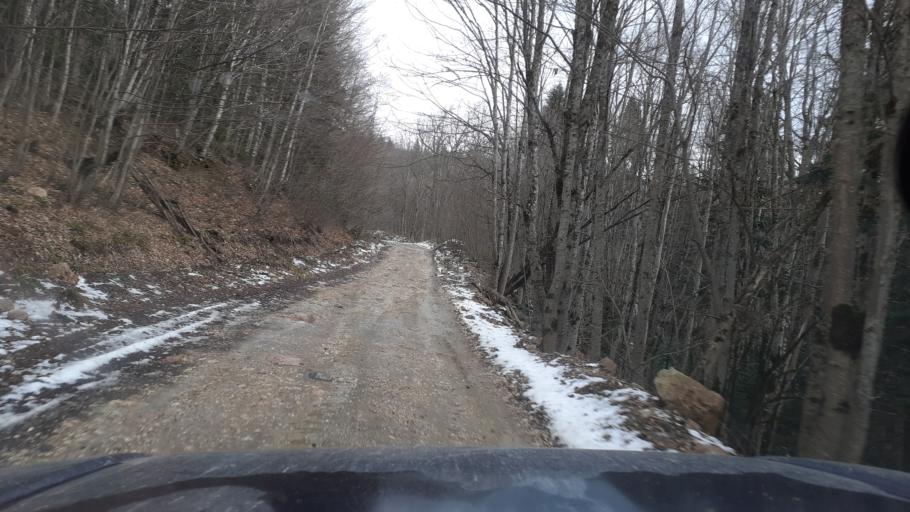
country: RU
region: Krasnodarskiy
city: Neftegorsk
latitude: 44.0785
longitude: 39.7527
